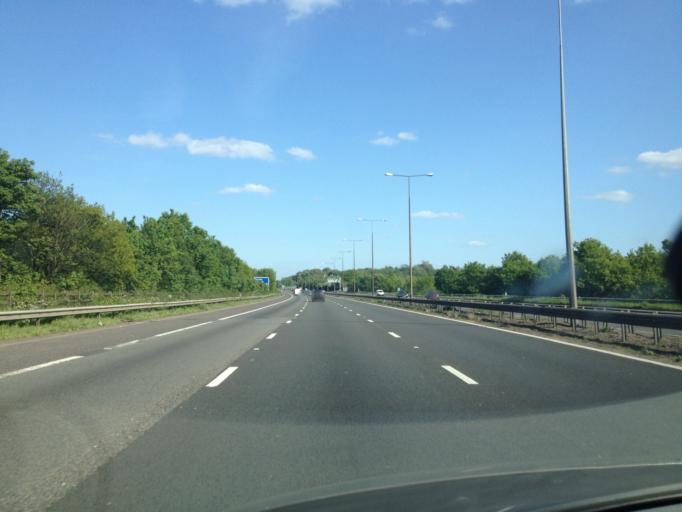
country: GB
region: England
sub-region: Hertfordshire
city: Elstree
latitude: 51.6405
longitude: -0.3180
